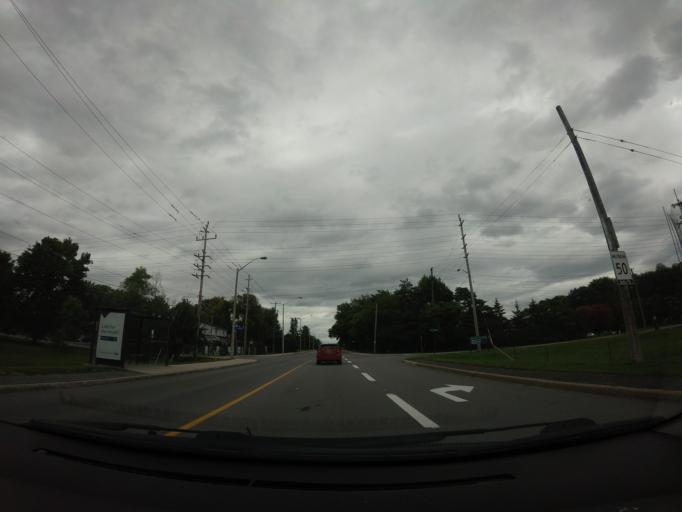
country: CA
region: Ontario
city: Ottawa
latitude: 45.4282
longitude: -75.5733
